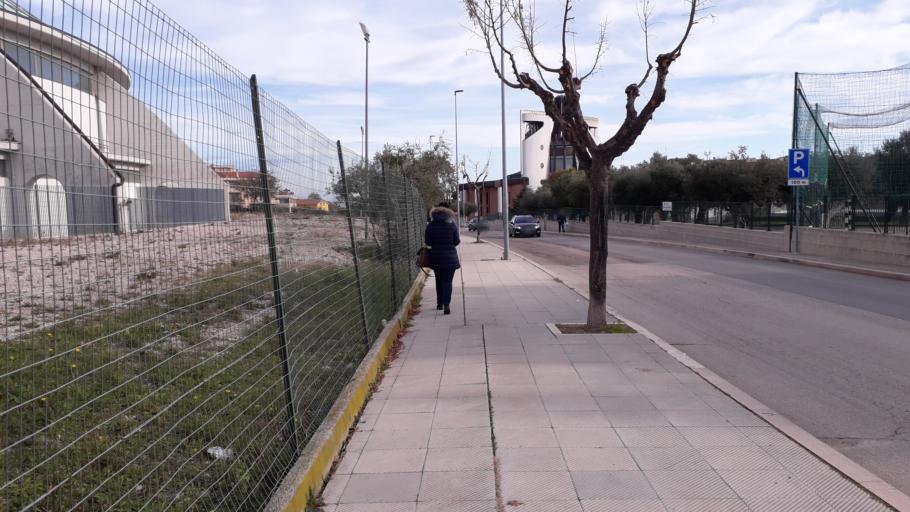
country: IT
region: Molise
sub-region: Provincia di Campobasso
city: Campomarino
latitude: 41.9507
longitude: 15.0323
